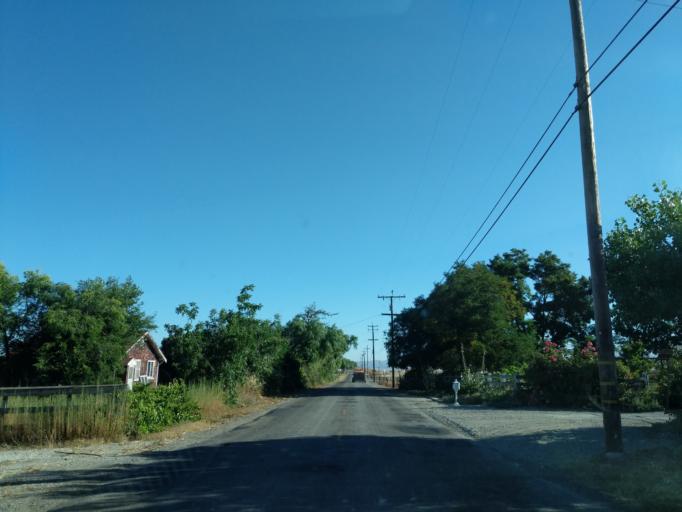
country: US
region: California
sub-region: San Benito County
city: Ridgemark
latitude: 36.8221
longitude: -121.3455
